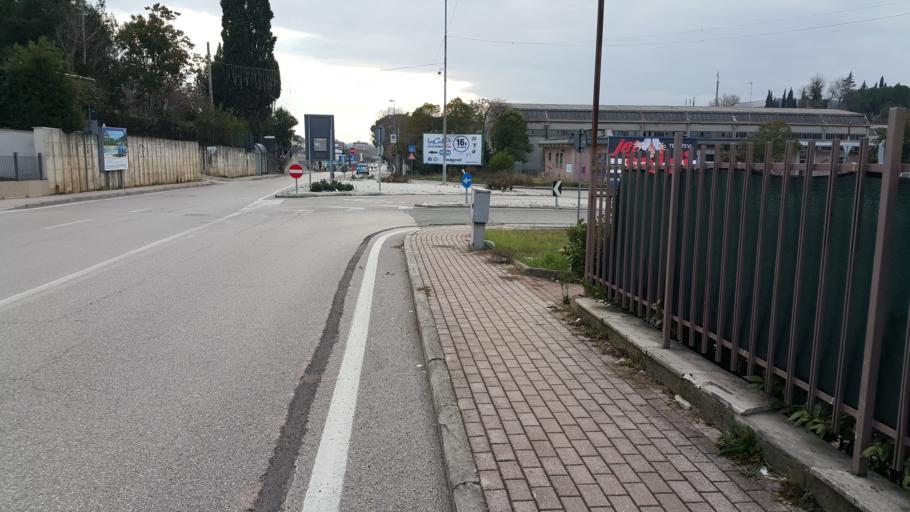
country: IT
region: Umbria
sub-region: Provincia di Perugia
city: Perugia
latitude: 43.0903
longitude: 12.3686
